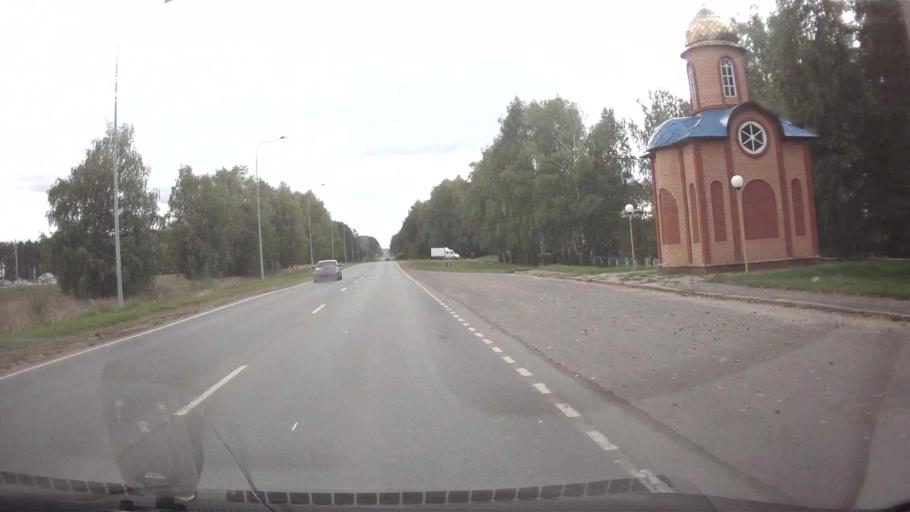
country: RU
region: Mariy-El
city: Kuzhener
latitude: 56.9932
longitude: 48.7429
